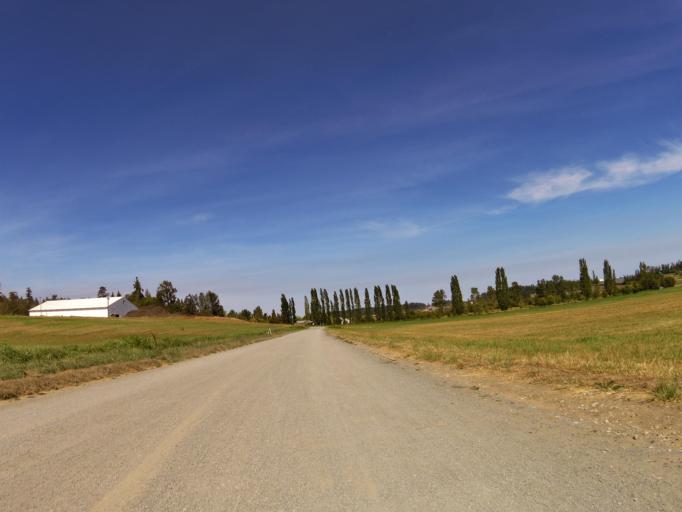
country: CA
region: British Columbia
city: North Saanich
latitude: 48.5550
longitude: -123.3863
